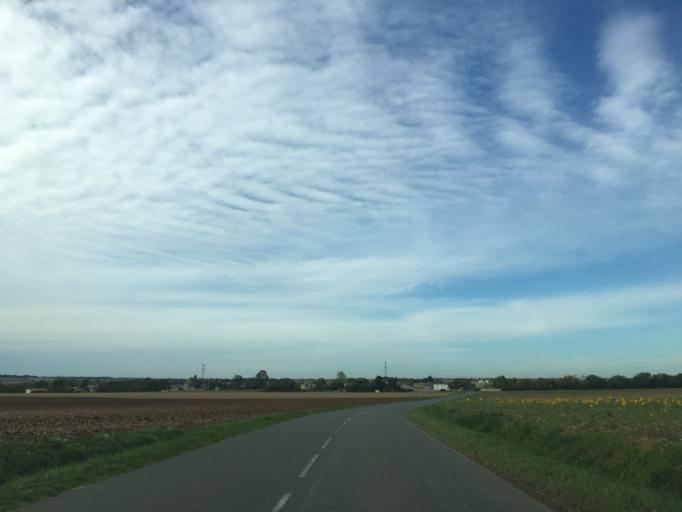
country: FR
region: Poitou-Charentes
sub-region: Departement de la Charente-Maritime
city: Aulnay
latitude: 46.0697
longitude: -0.4485
